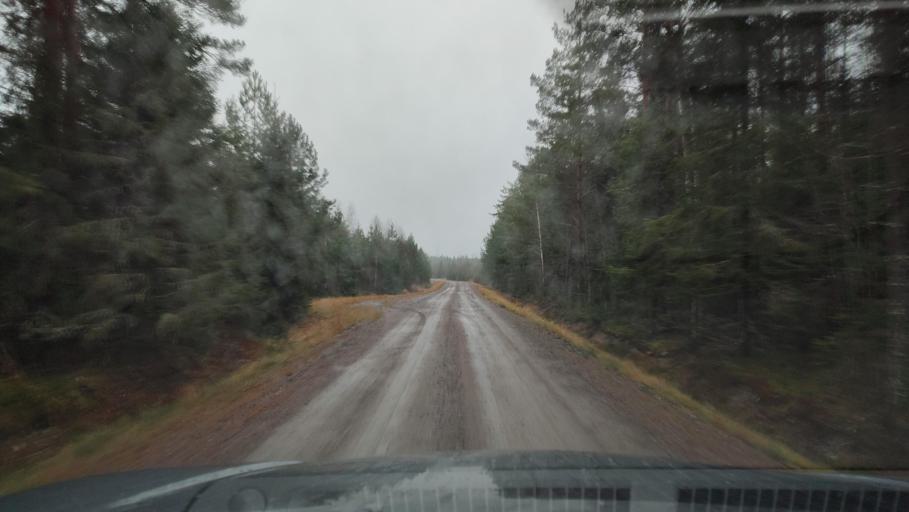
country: FI
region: Southern Ostrobothnia
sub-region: Suupohja
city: Karijoki
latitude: 62.2193
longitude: 21.7411
